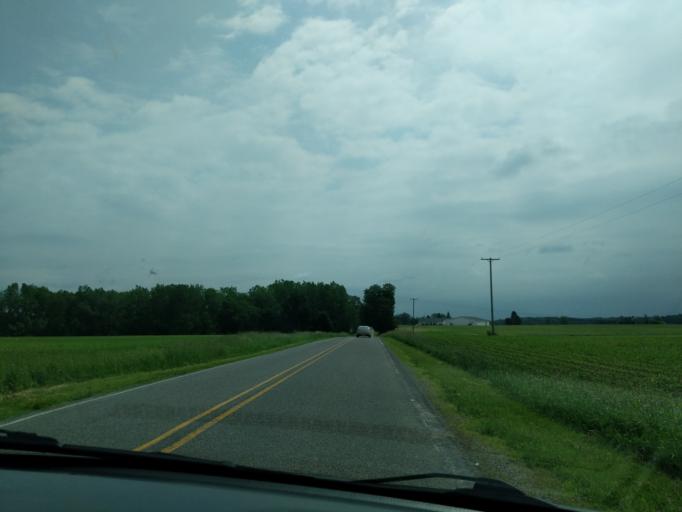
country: US
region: Michigan
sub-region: Ingham County
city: Williamston
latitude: 42.6933
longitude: -84.2282
